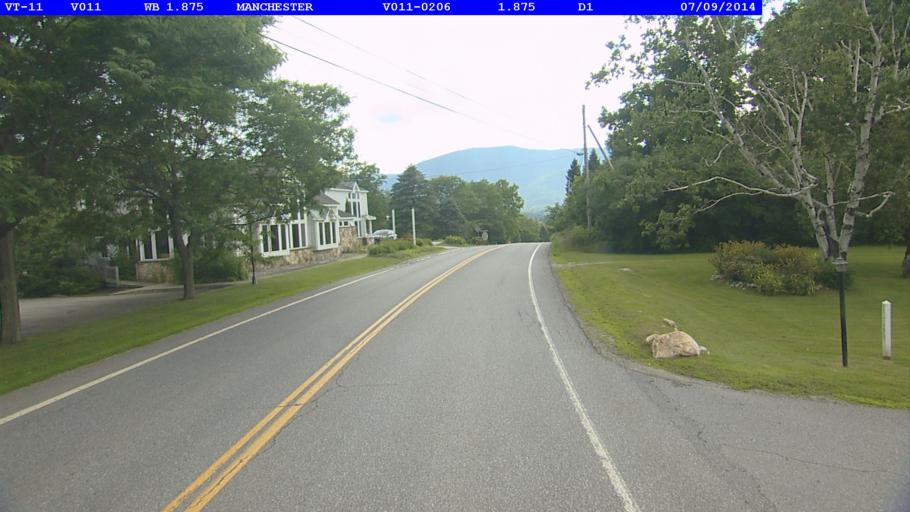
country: US
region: Vermont
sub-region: Bennington County
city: Manchester Center
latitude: 43.1739
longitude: -73.0224
